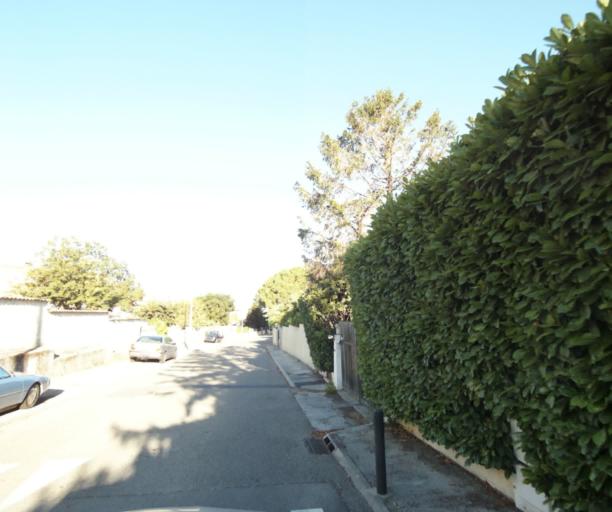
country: FR
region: Languedoc-Roussillon
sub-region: Departement du Gard
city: Bouillargues
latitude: 43.8016
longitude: 4.4229
